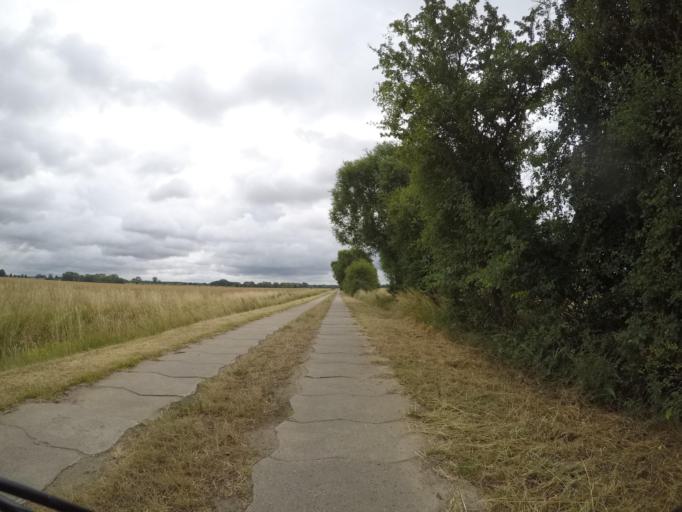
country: DE
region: Lower Saxony
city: Damnatz
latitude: 53.1785
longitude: 11.1185
